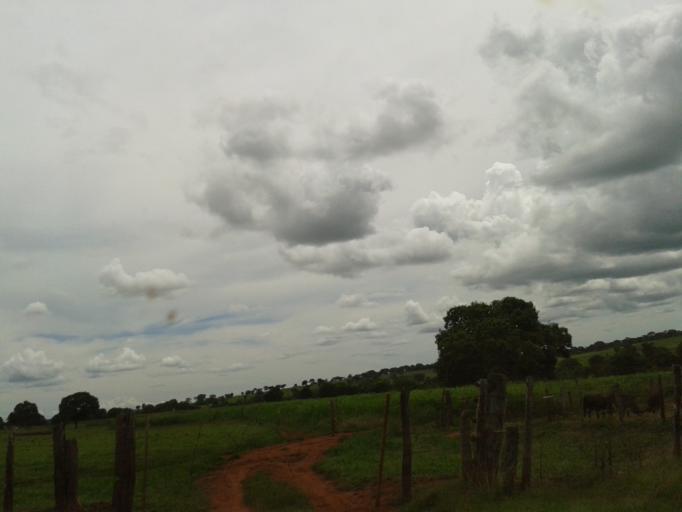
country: BR
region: Minas Gerais
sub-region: Santa Vitoria
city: Santa Vitoria
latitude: -18.7891
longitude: -49.8560
